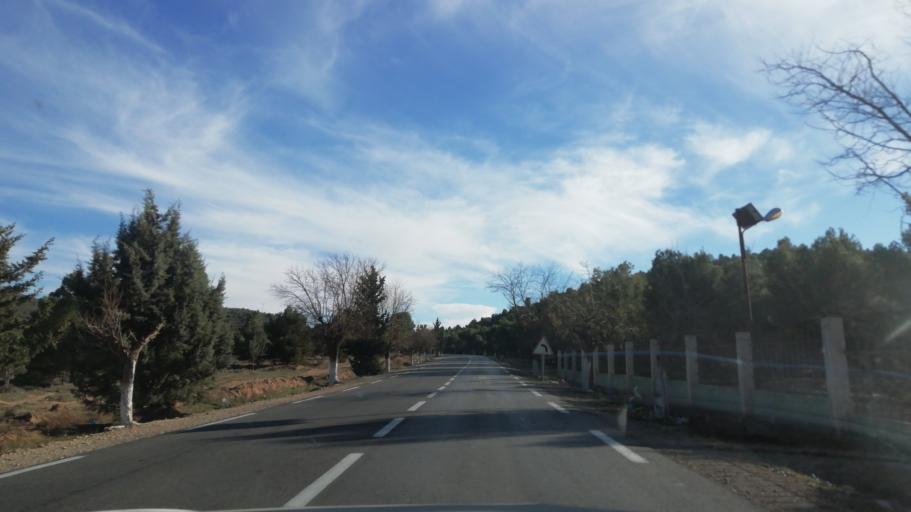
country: DZ
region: Tlemcen
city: Sebdou
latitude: 34.6128
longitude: -1.3320
